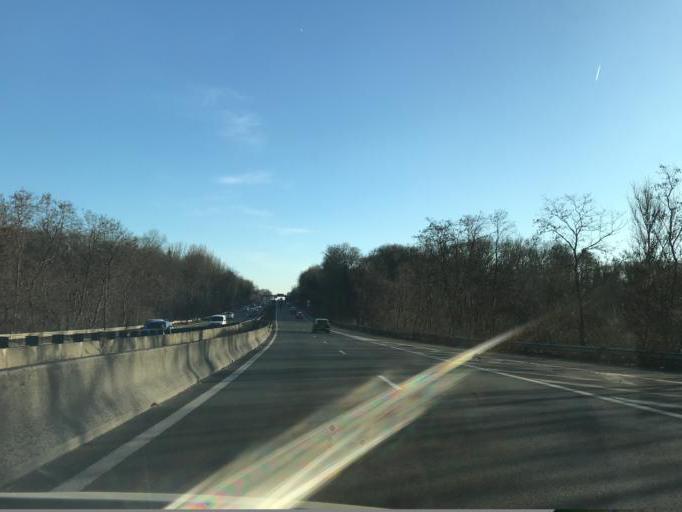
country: FR
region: Ile-de-France
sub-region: Departement de Seine-et-Marne
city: Servon
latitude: 48.7234
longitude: 2.5976
